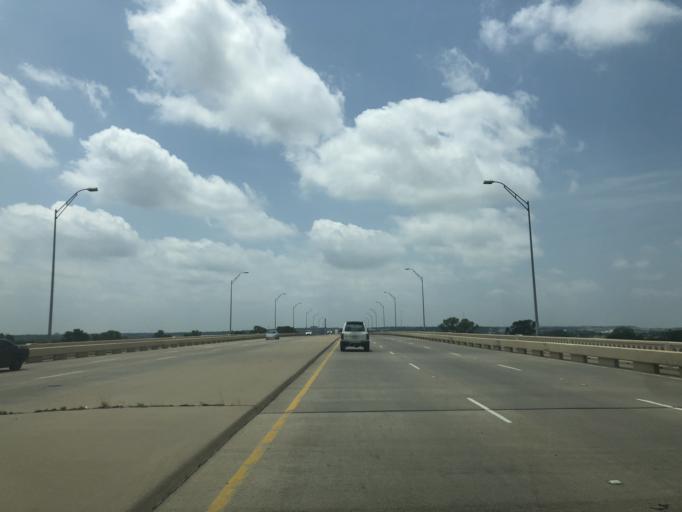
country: US
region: Texas
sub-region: Dallas County
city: Dallas
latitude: 32.8003
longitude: -96.8541
